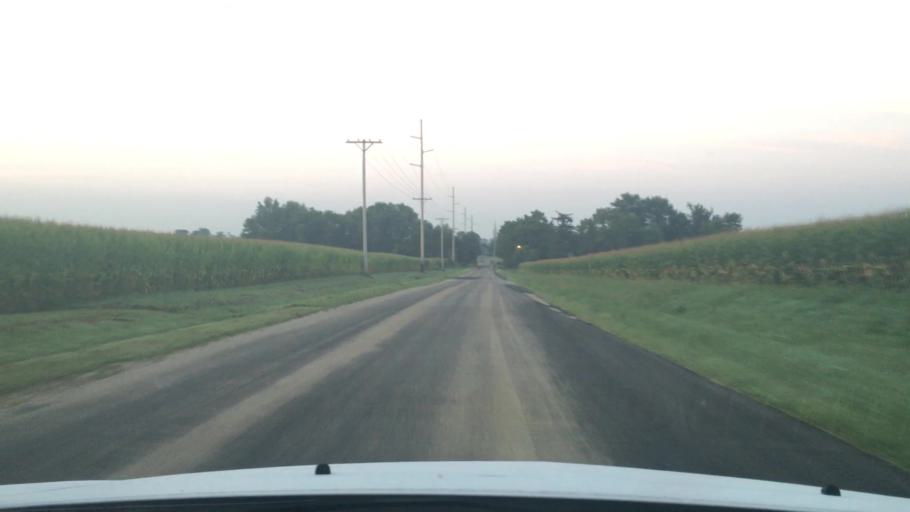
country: US
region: Illinois
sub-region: Ogle County
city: Rochelle
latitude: 41.9121
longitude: -89.0000
